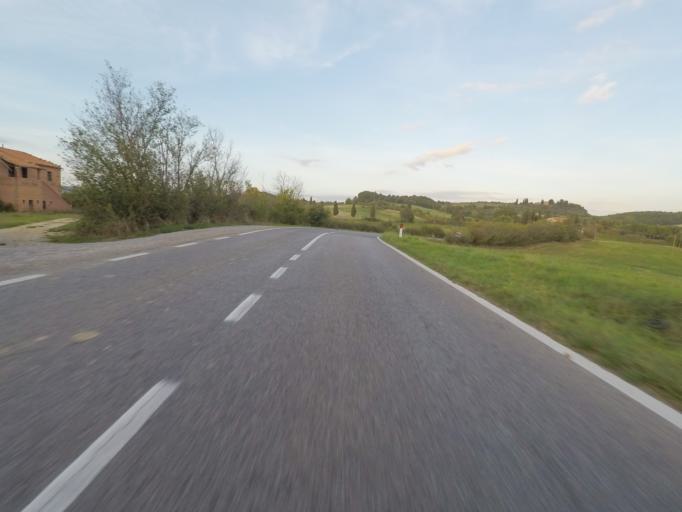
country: IT
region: Tuscany
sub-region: Provincia di Siena
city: Pienza
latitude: 43.0962
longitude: 11.6906
